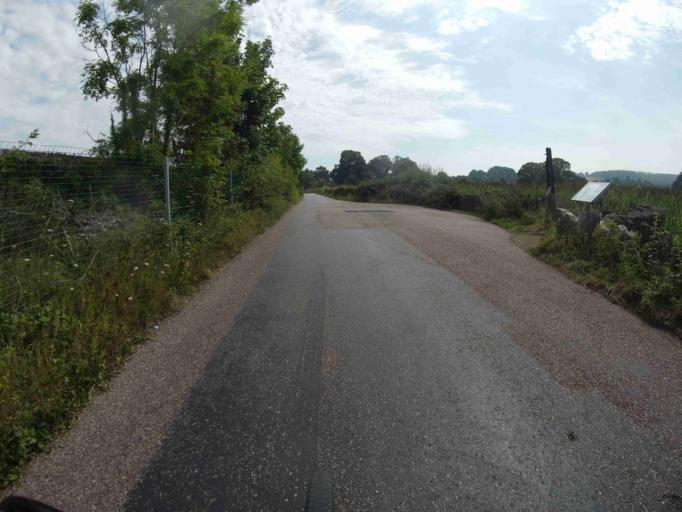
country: GB
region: England
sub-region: Devon
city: Starcross
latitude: 50.6422
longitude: -3.4527
